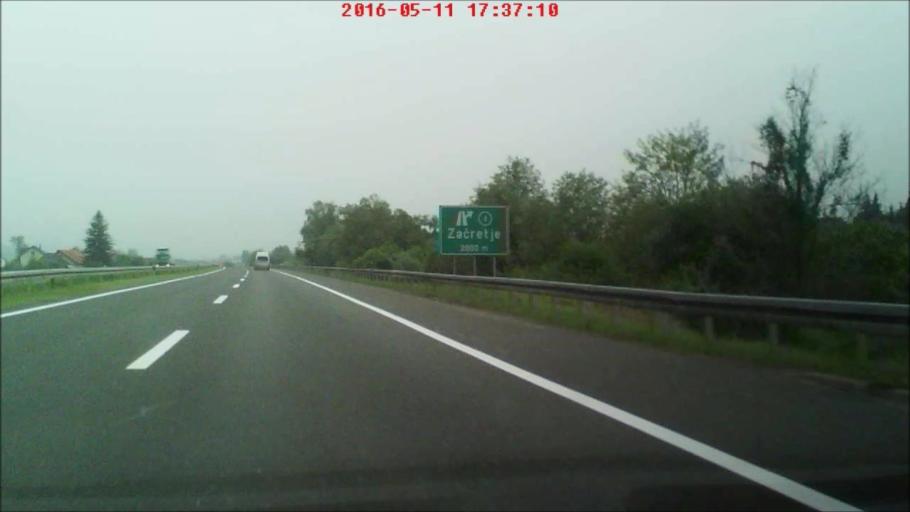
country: HR
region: Krapinsko-Zagorska
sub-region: Grad Krapina
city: Krapina
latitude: 46.1061
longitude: 15.8949
